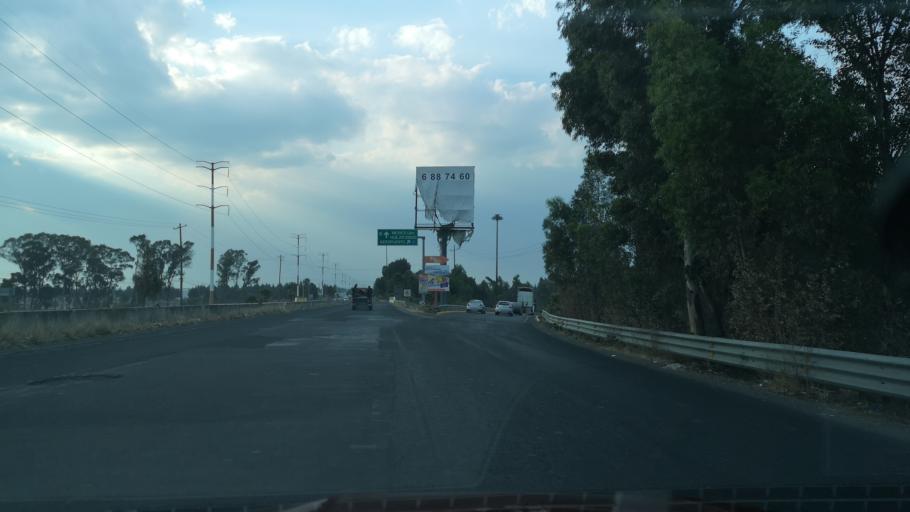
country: MX
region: Puebla
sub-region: Juan C. Bonilla
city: Santa Maria Zacatepec
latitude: 19.1313
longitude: -98.3726
